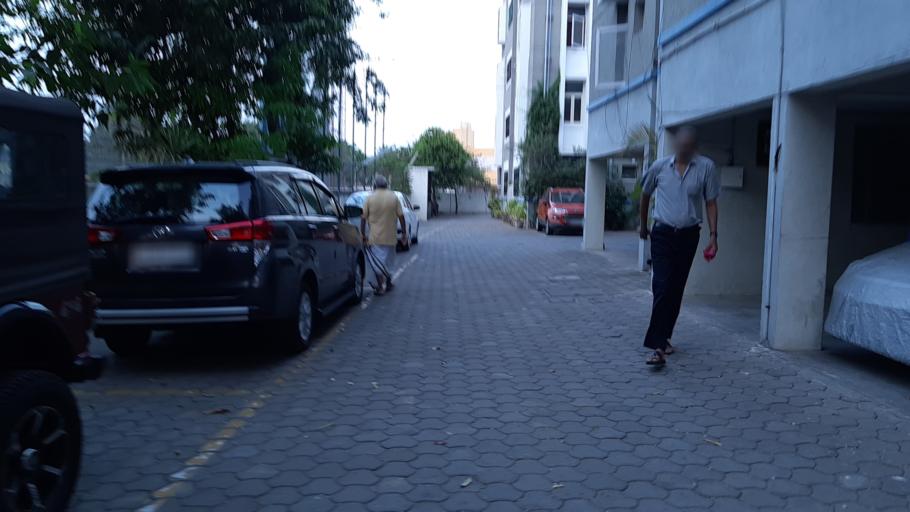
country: IN
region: Tamil Nadu
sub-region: Kancheepuram
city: Alandur
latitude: 13.0079
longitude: 80.2191
